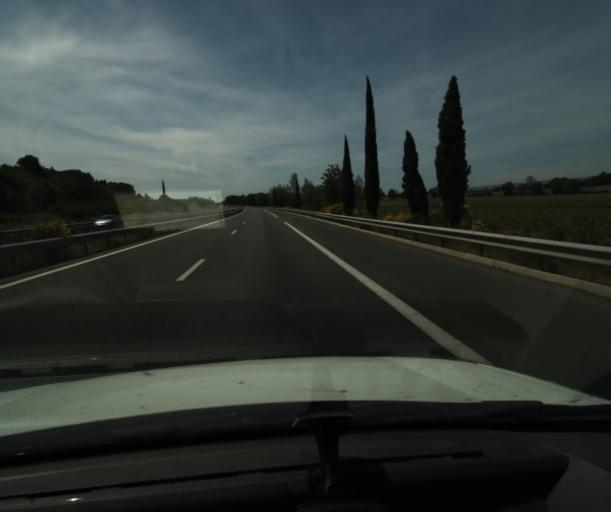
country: FR
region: Languedoc-Roussillon
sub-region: Departement de l'Aude
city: Lavalette
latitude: 43.2010
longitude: 2.2777
